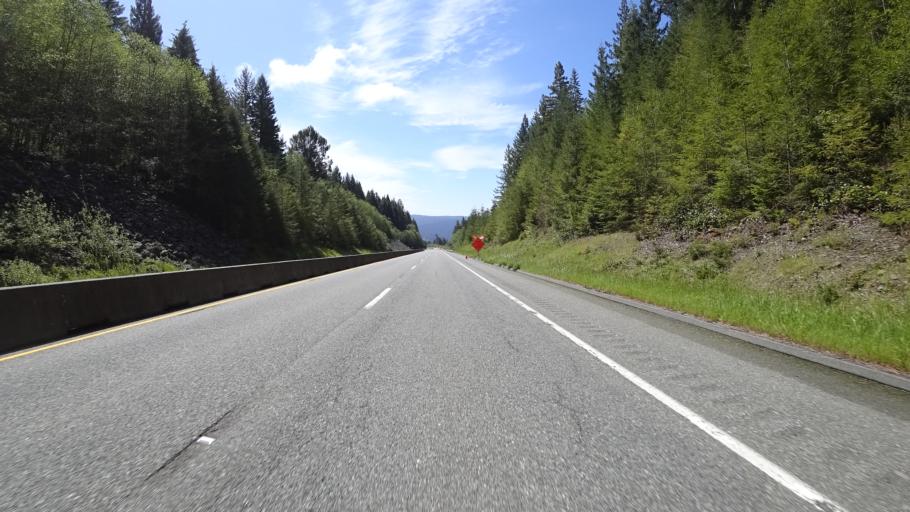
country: US
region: California
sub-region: Humboldt County
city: Westhaven-Moonstone
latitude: 41.3844
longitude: -123.9950
